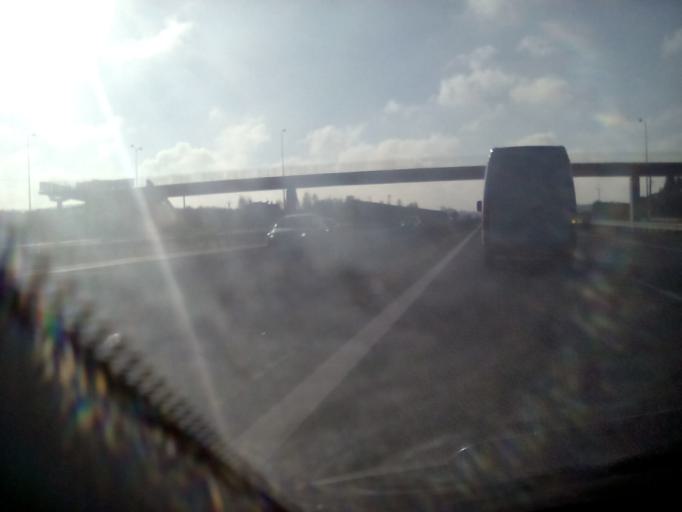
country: PL
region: Masovian Voivodeship
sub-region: Powiat grojecki
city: Grojec
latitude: 51.8147
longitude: 20.8841
